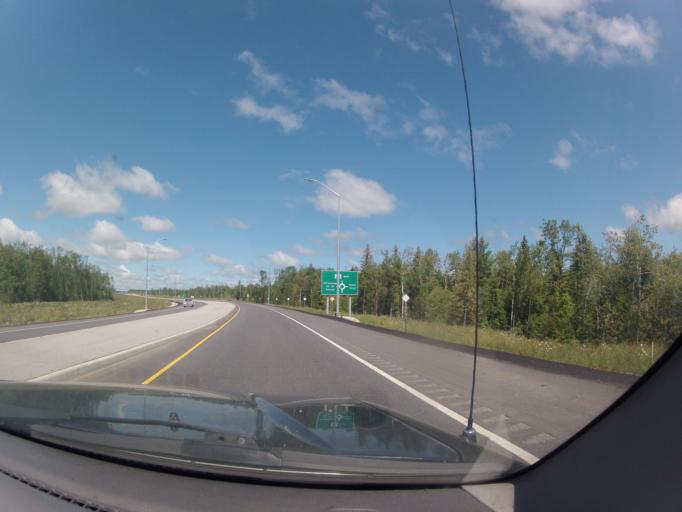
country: CA
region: Ontario
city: Wasaga Beach
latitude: 44.4598
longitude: -80.1072
